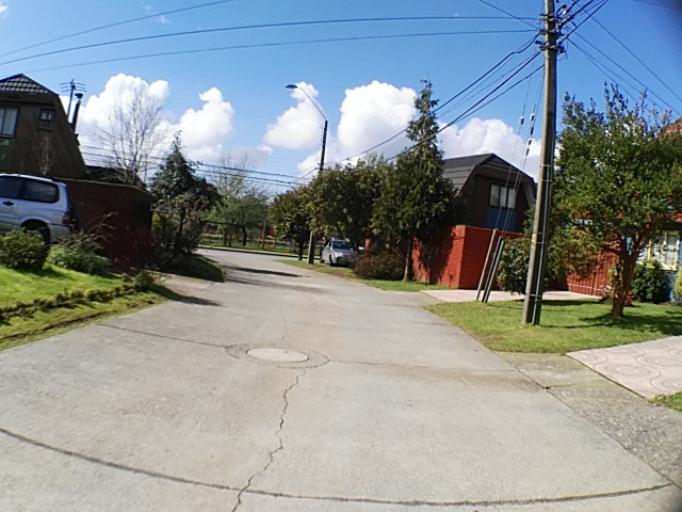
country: CL
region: Los Rios
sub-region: Provincia de Valdivia
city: Valdivia
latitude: -39.8337
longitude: -73.2290
